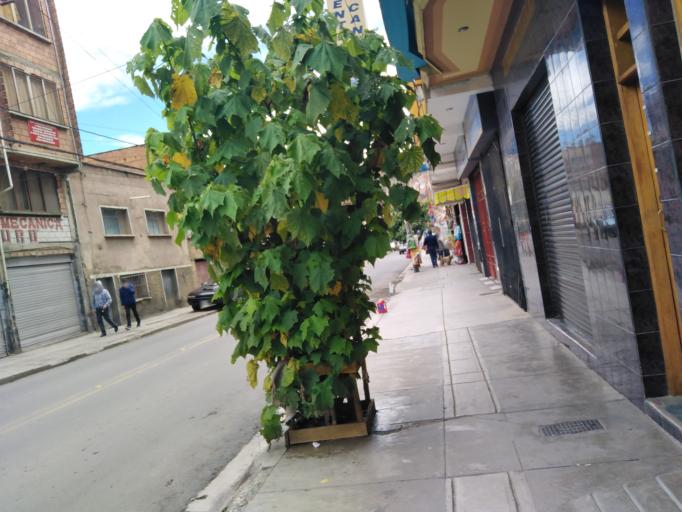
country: BO
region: La Paz
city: La Paz
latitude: -16.5101
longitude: -68.1410
